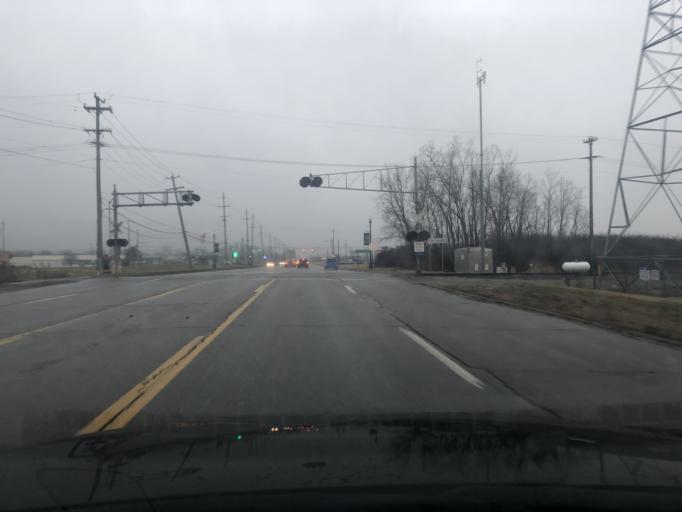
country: US
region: Michigan
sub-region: Wayne County
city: Woodhaven
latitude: 42.1283
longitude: -83.2258
